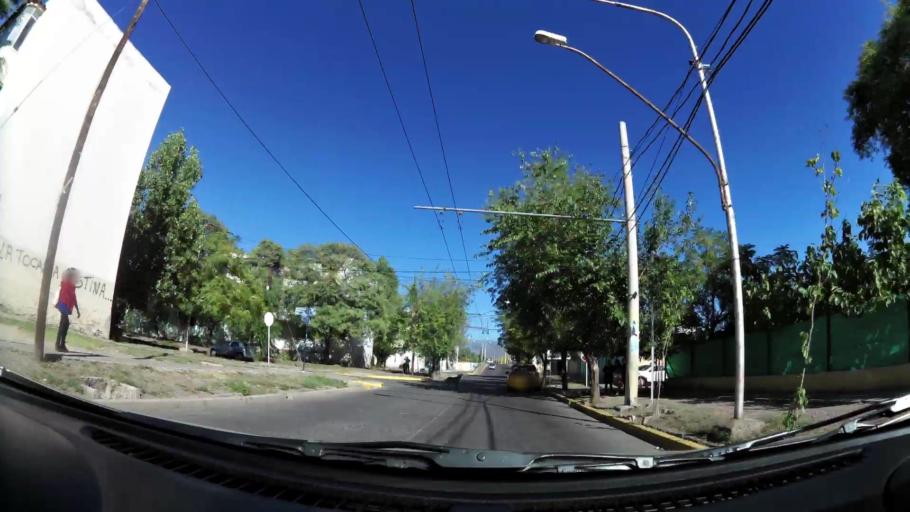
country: AR
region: Mendoza
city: Las Heras
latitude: -32.8687
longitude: -68.8590
